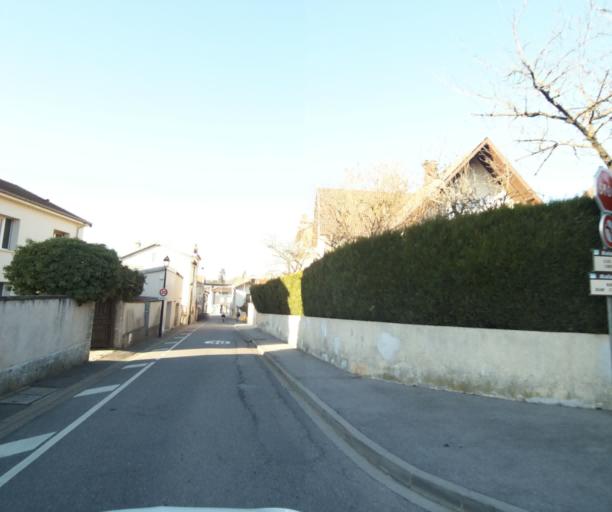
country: FR
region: Lorraine
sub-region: Departement de Meurthe-et-Moselle
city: Malzeville
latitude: 48.7144
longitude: 6.1854
